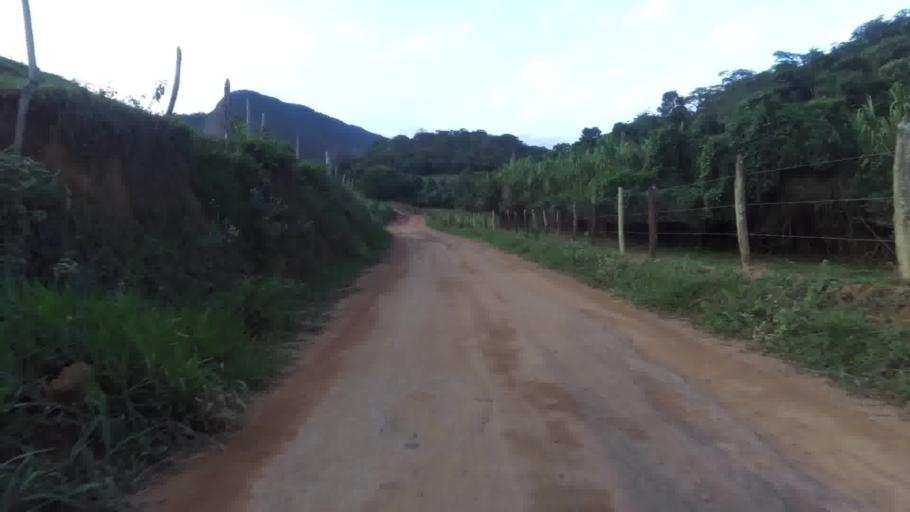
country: BR
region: Espirito Santo
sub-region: Guarapari
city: Guarapari
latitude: -20.6895
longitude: -40.6287
